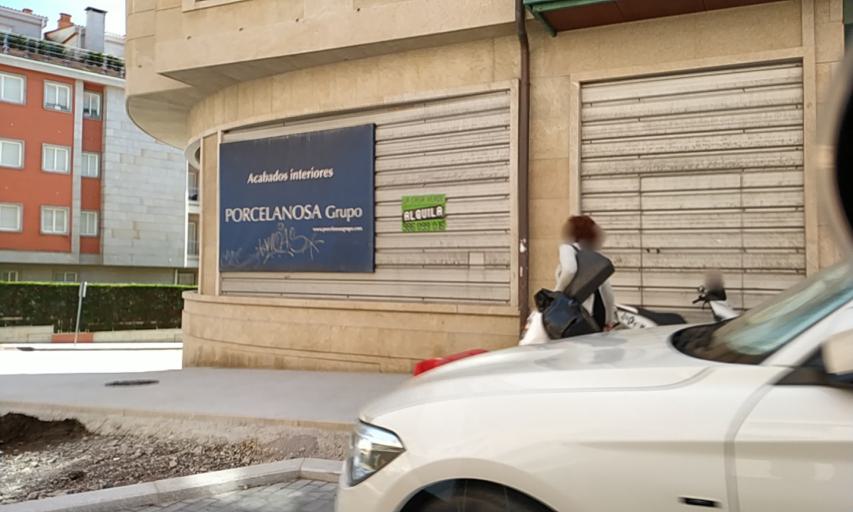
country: ES
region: Galicia
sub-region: Provincia de Pontevedra
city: Sanxenxo
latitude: 42.4039
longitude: -8.8098
